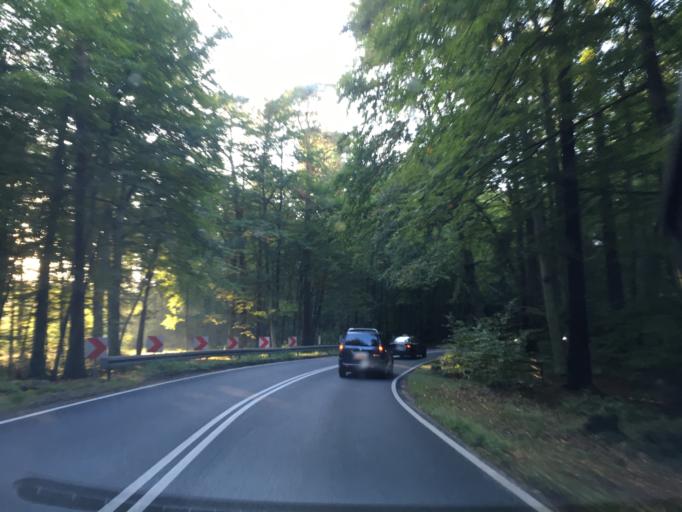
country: PL
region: Pomeranian Voivodeship
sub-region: Gdynia
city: Wielki Kack
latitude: 54.4562
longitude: 18.5161
